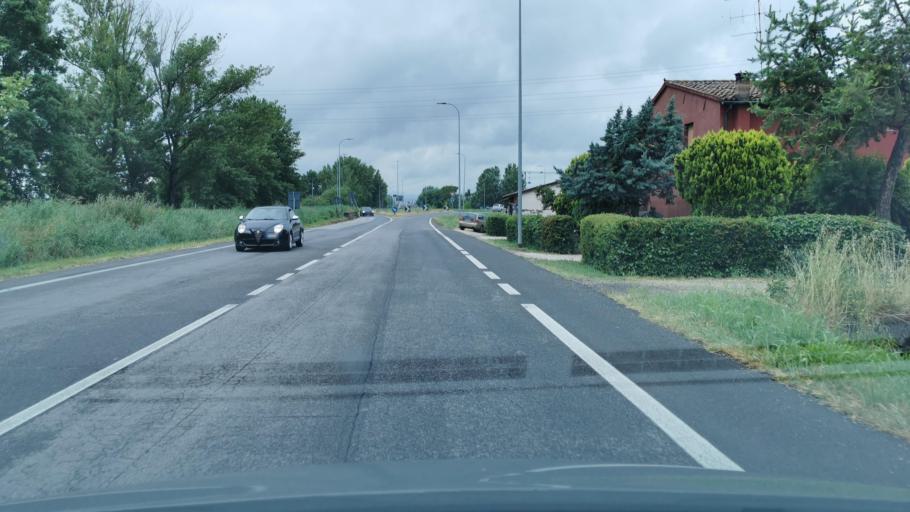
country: IT
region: Emilia-Romagna
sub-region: Provincia di Ravenna
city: Granarolo
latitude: 44.3280
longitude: 11.9101
